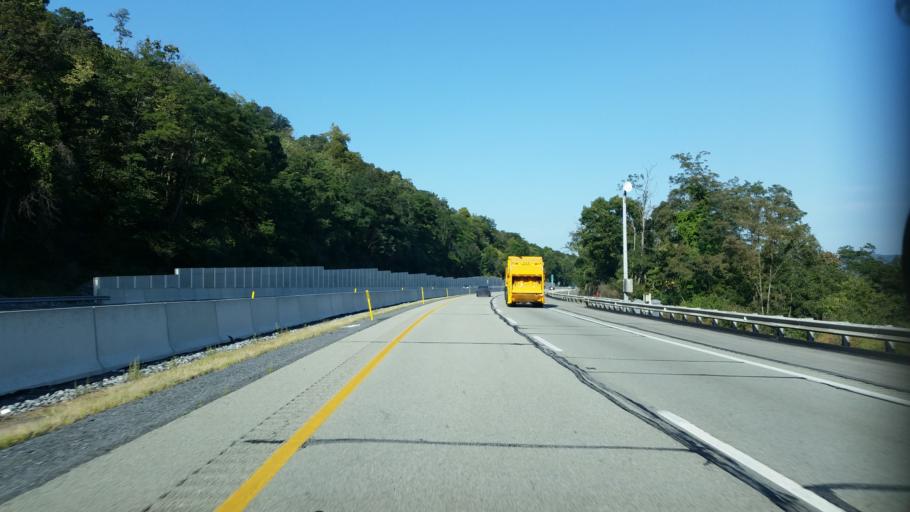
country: US
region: Pennsylvania
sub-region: Fulton County
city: McConnellsburg
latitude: 40.0487
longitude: -78.1180
